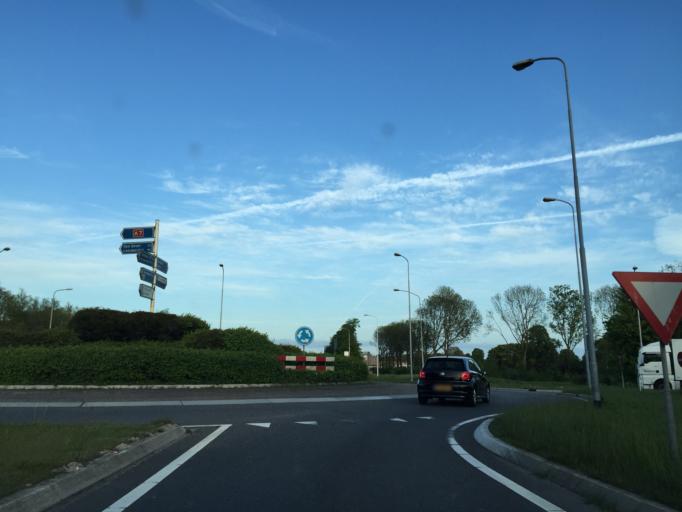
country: NL
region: North Holland
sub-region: Gemeente Hoorn
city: Hoorn
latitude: 52.6481
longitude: 5.0363
